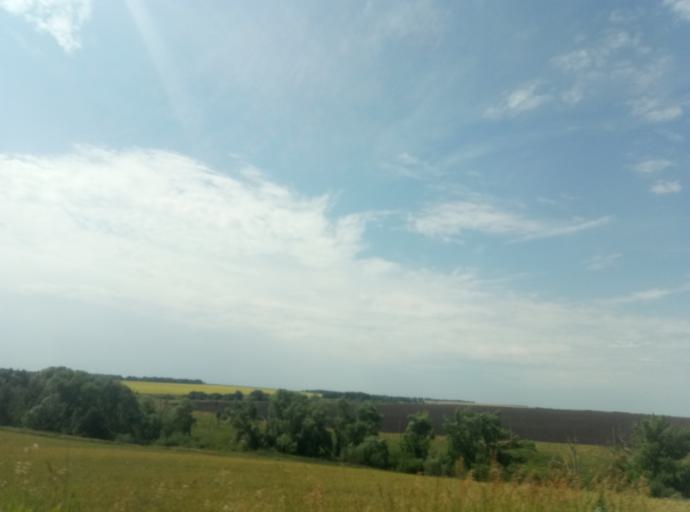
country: RU
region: Tula
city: Kireyevsk
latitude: 53.9096
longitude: 37.9690
